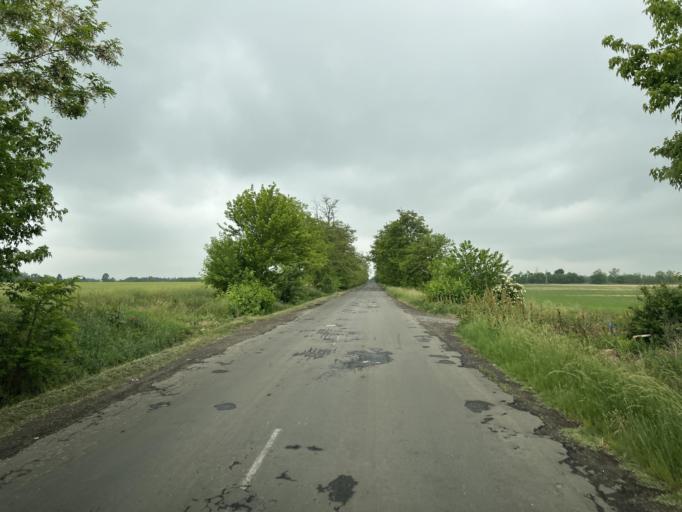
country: HU
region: Pest
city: Tura
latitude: 47.6221
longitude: 19.6241
